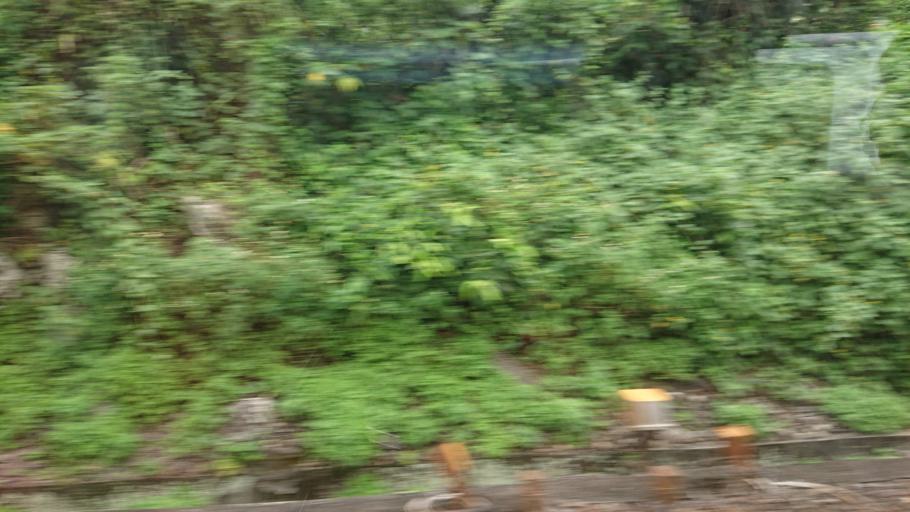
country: TW
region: Taiwan
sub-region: Yilan
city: Yilan
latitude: 24.9091
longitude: 121.8743
